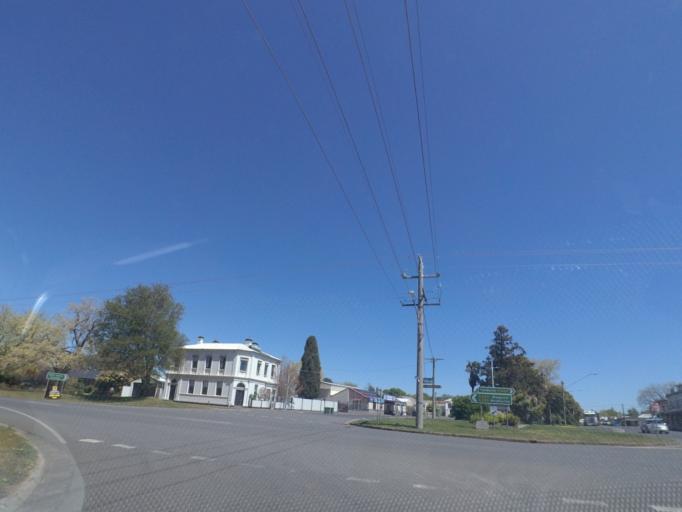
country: AU
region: Victoria
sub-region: Hume
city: Sunbury
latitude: -37.2775
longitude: 144.7368
